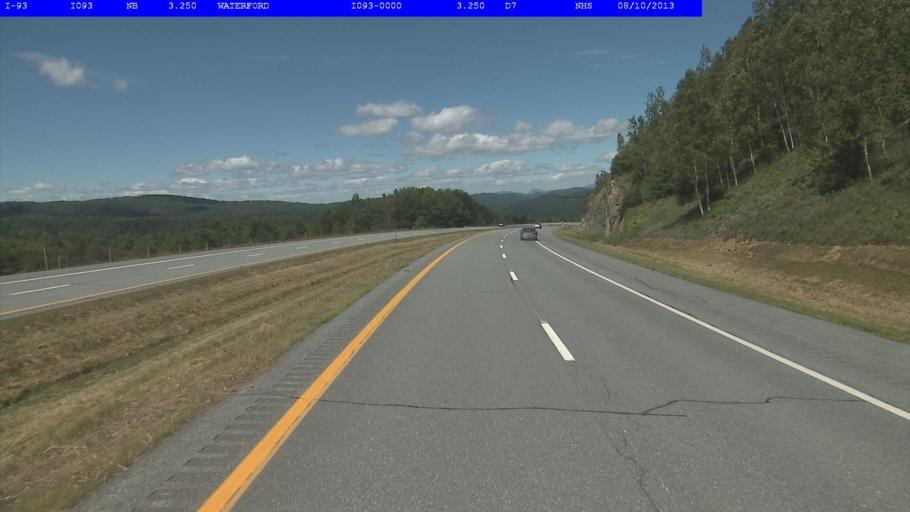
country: US
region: Vermont
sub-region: Caledonia County
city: Saint Johnsbury
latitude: 44.3826
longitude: -71.9225
